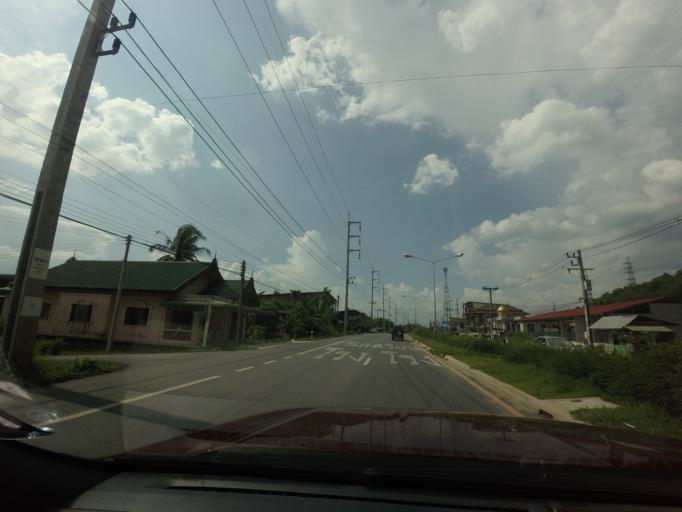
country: TH
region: Yala
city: Yala
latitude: 6.4955
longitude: 101.2656
